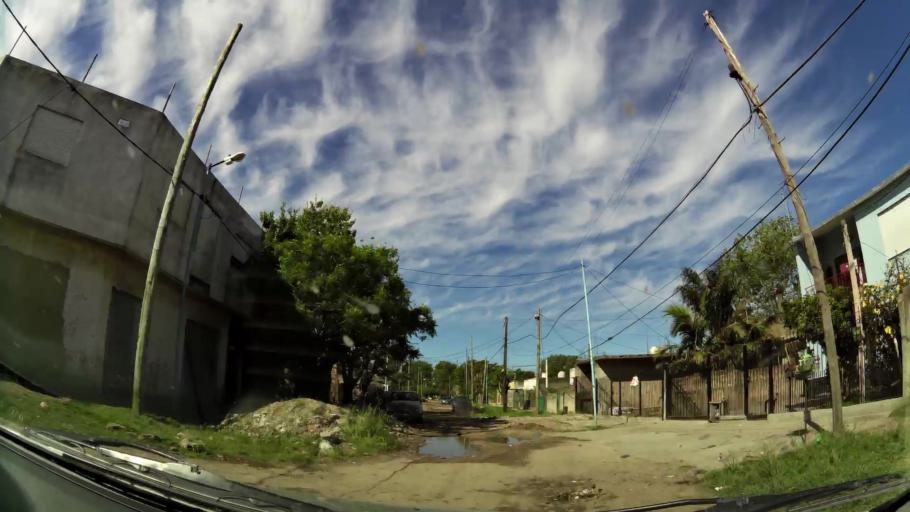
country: AR
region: Buenos Aires
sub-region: Partido de Quilmes
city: Quilmes
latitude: -34.7662
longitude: -58.3031
